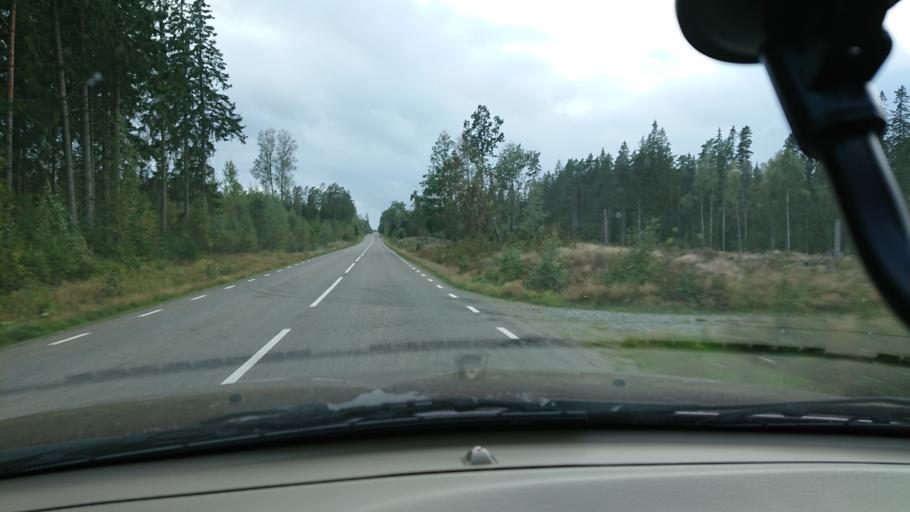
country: SE
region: Kronoberg
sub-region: Vaxjo Kommun
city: Lammhult
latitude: 57.0968
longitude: 14.6777
